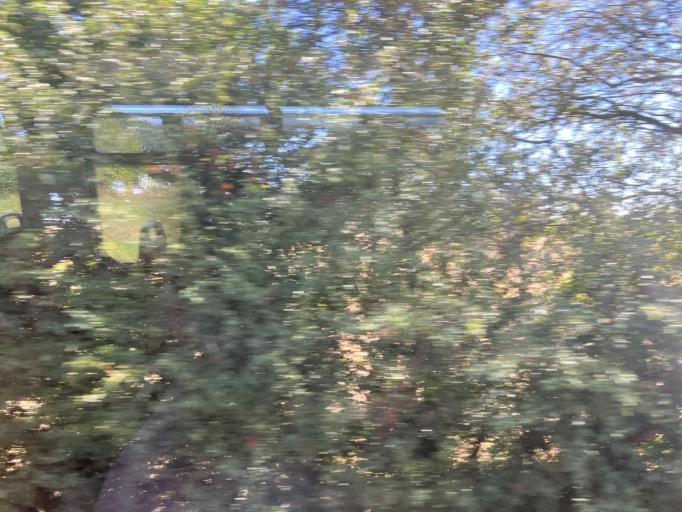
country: GB
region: England
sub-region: Lincolnshire
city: Spilsby
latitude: 53.0855
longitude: 0.0916
